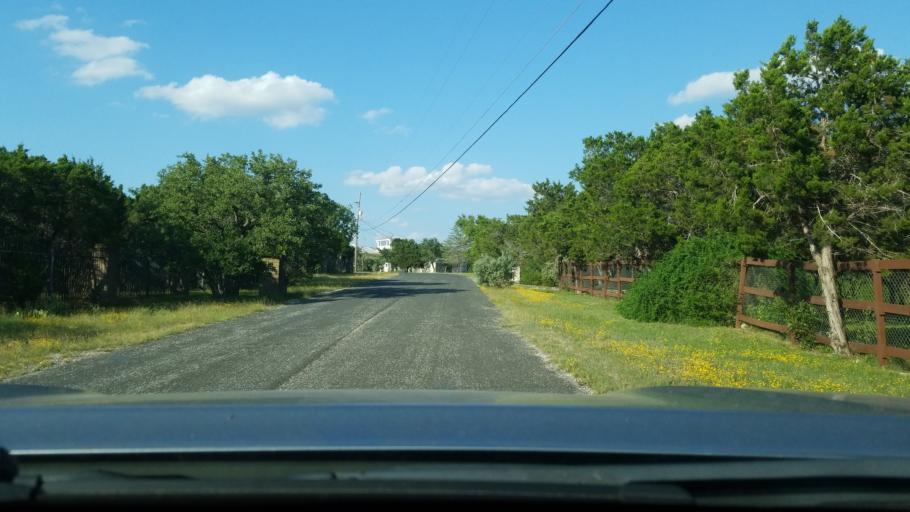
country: US
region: Texas
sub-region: Bexar County
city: Timberwood Park
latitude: 29.7060
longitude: -98.4448
